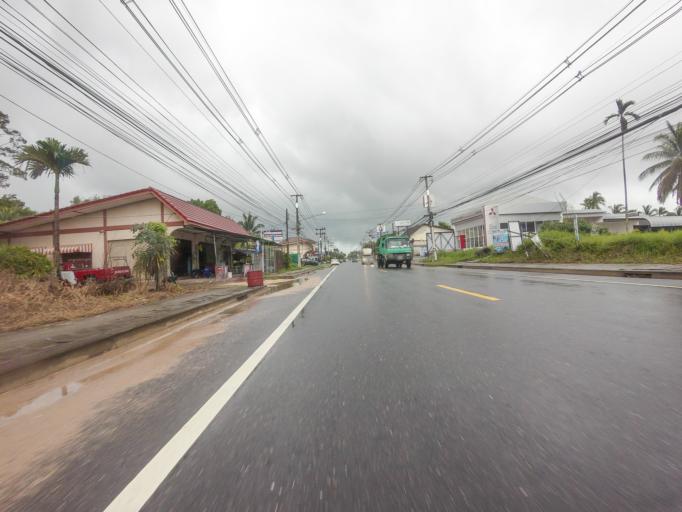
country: TH
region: Surat Thani
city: Ko Samui
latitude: 9.4483
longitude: 100.0043
